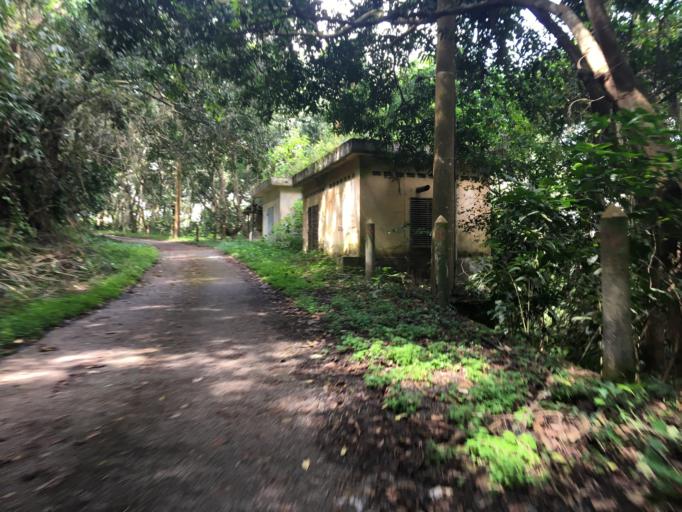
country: TG
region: Plateaux
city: Kpalime
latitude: 6.9526
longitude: 0.5823
